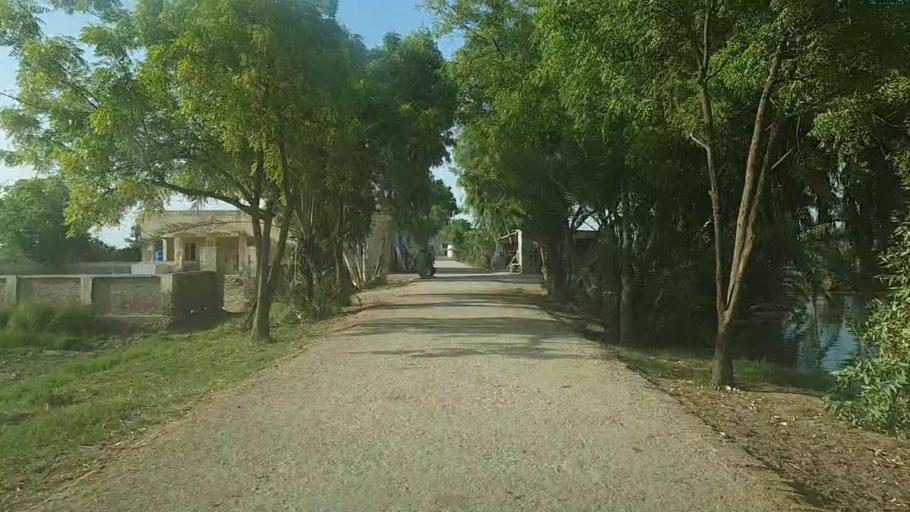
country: PK
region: Sindh
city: Khairpur
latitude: 28.1120
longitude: 69.6376
